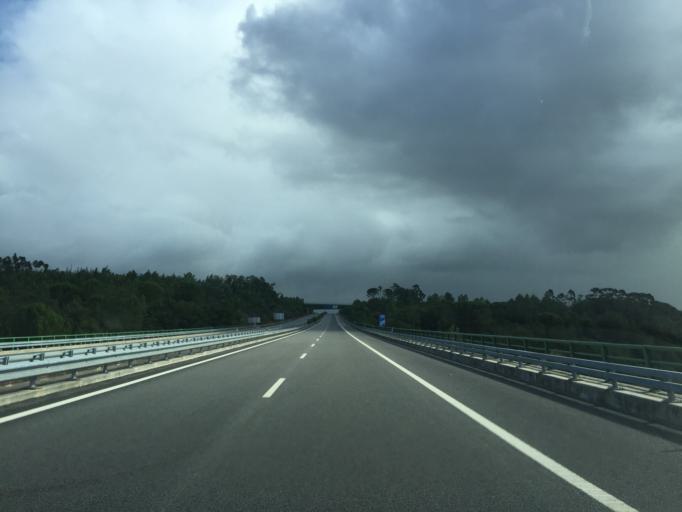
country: PT
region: Coimbra
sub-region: Cantanhede
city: Cantanhede
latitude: 40.2841
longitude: -8.5381
